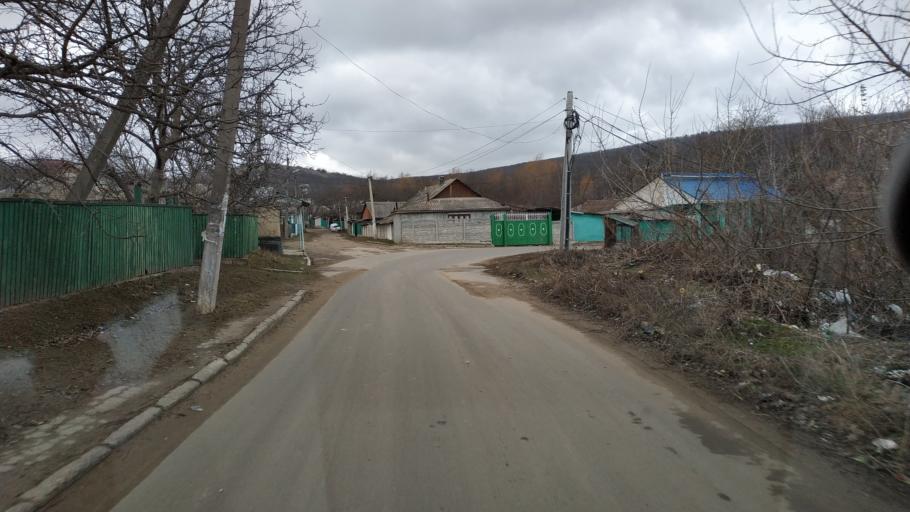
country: MD
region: Calarasi
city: Calarasi
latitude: 47.2103
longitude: 28.2555
